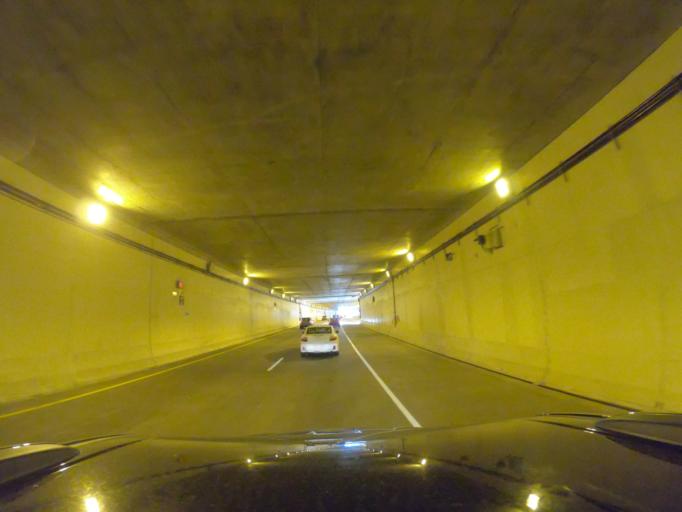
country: US
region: New Jersey
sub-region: Mercer County
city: Trenton
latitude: 40.1956
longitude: -74.7579
